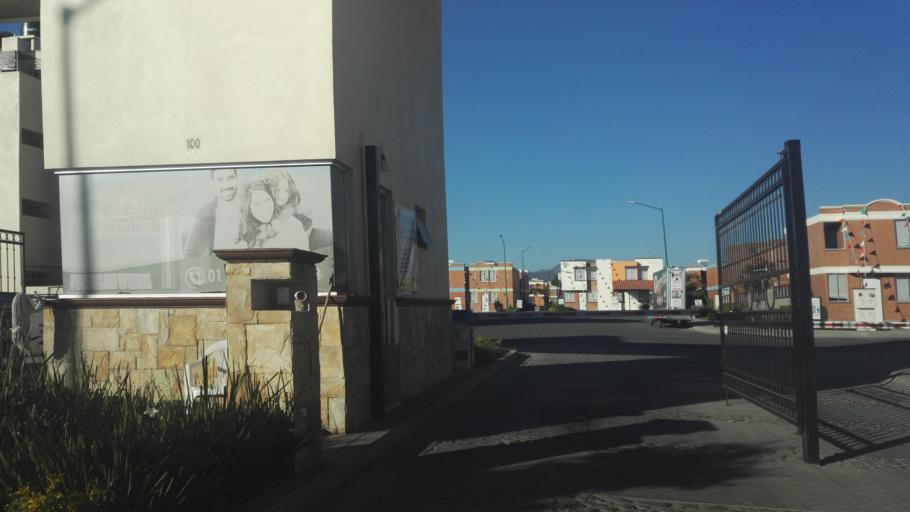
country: MX
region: Guanajuato
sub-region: Leon
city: Fraccionamiento Paraiso Real
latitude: 21.0646
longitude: -101.6088
